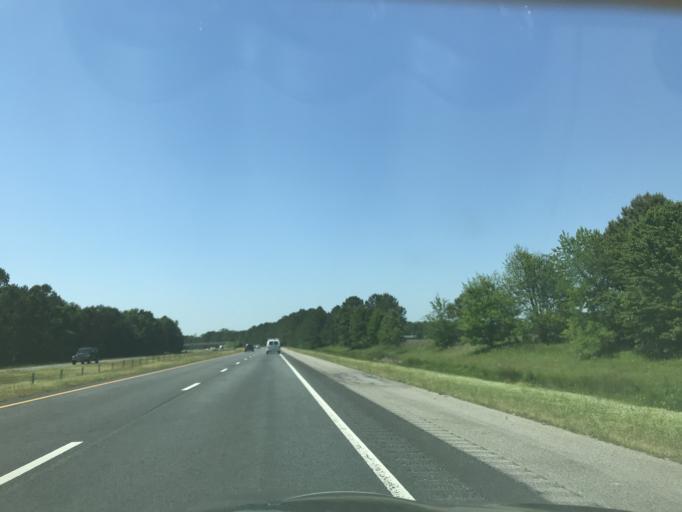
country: US
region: North Carolina
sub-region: Johnston County
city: Benson
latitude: 35.3364
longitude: -78.4612
